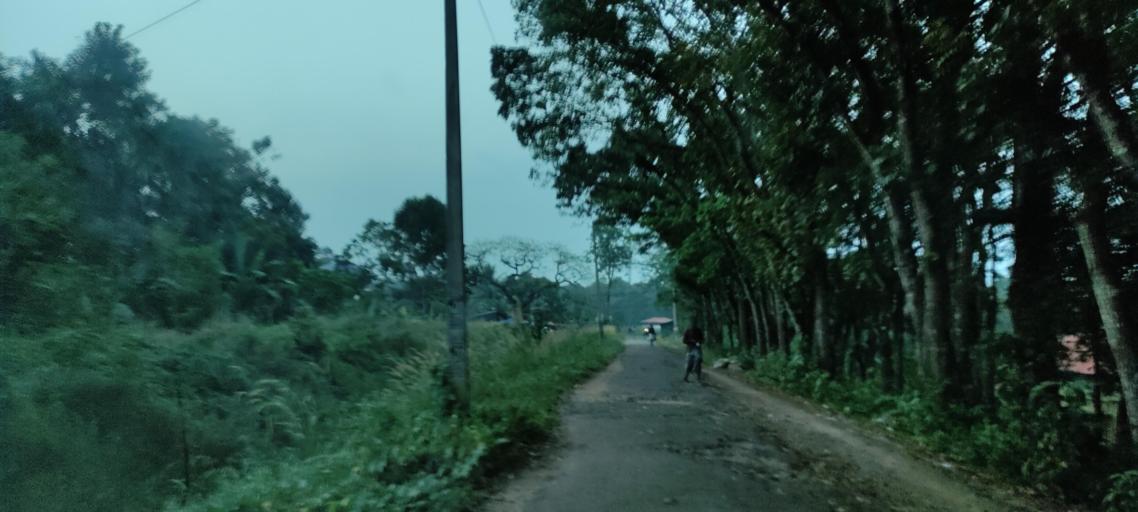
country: IN
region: Kerala
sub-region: Pattanamtitta
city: Adur
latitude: 9.1615
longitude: 76.7451
